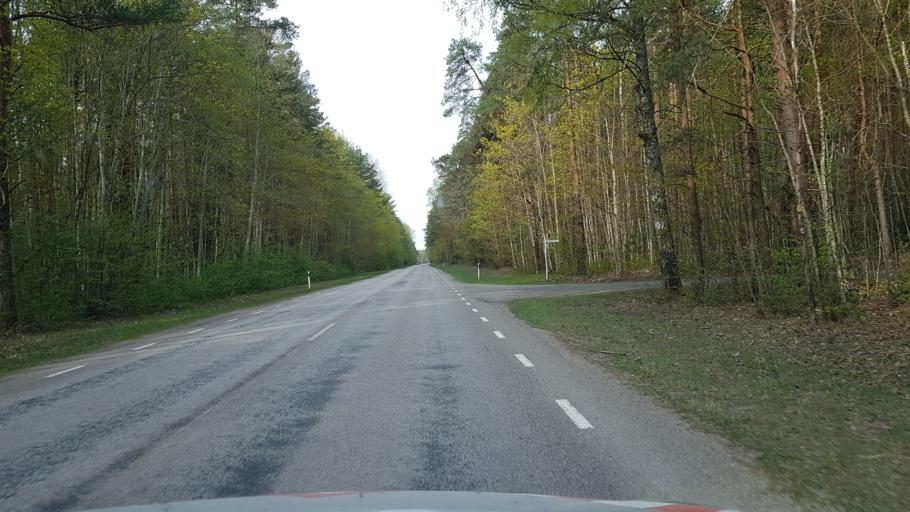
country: EE
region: Paernumaa
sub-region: Audru vald
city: Audru
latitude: 58.4117
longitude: 24.3473
